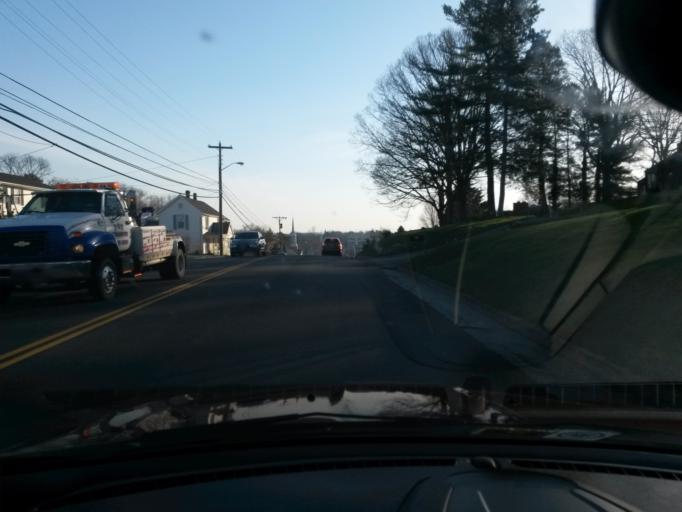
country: US
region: Virginia
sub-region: Montgomery County
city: Christiansburg
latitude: 37.1249
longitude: -80.4146
